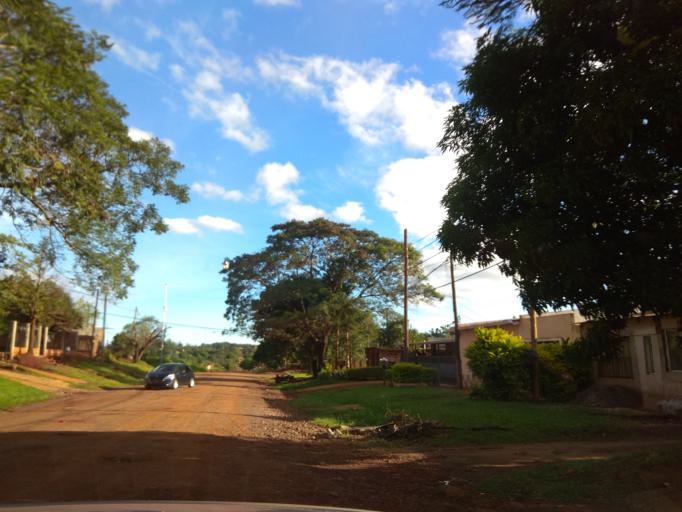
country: AR
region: Misiones
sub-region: Departamento de Capital
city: Posadas
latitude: -27.3907
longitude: -55.9274
